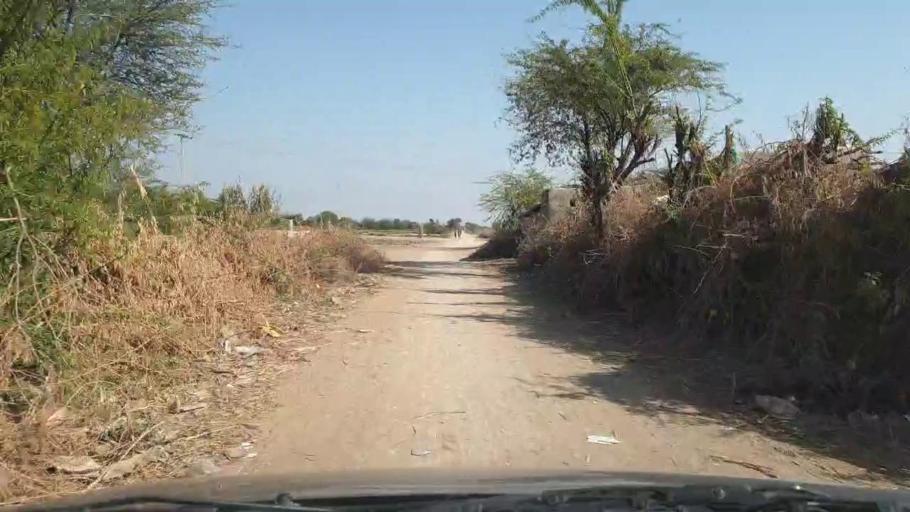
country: PK
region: Sindh
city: Samaro
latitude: 25.2004
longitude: 69.2653
